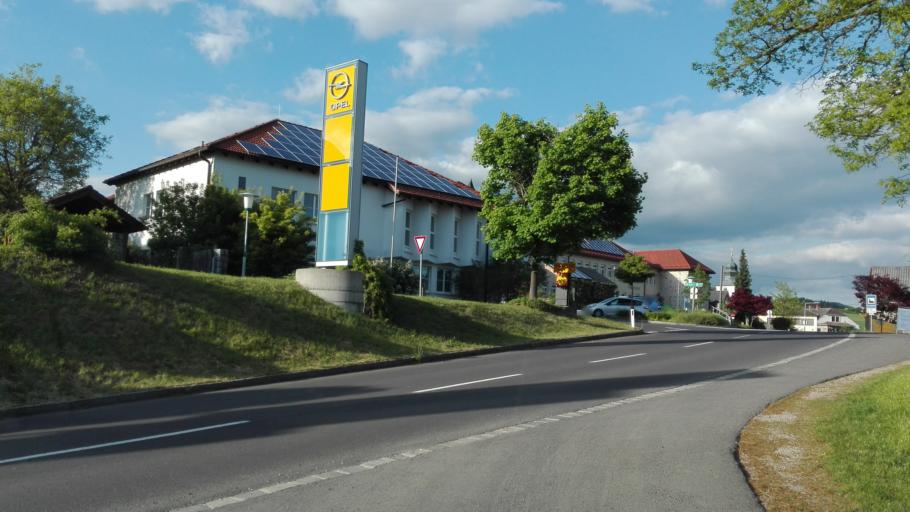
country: AT
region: Upper Austria
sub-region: Politischer Bezirk Freistadt
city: Freistadt
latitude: 48.4154
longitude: 14.6102
